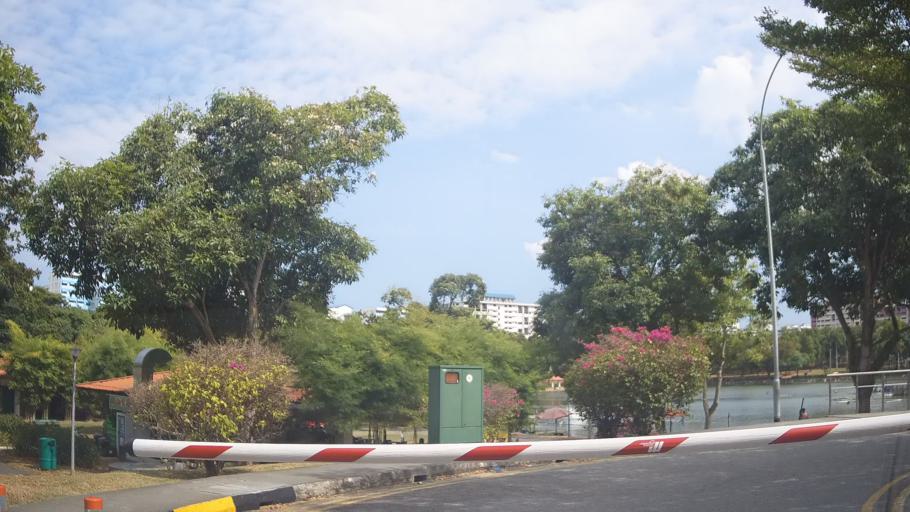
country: MY
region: Johor
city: Kampung Pasir Gudang Baru
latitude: 1.3728
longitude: 103.9514
